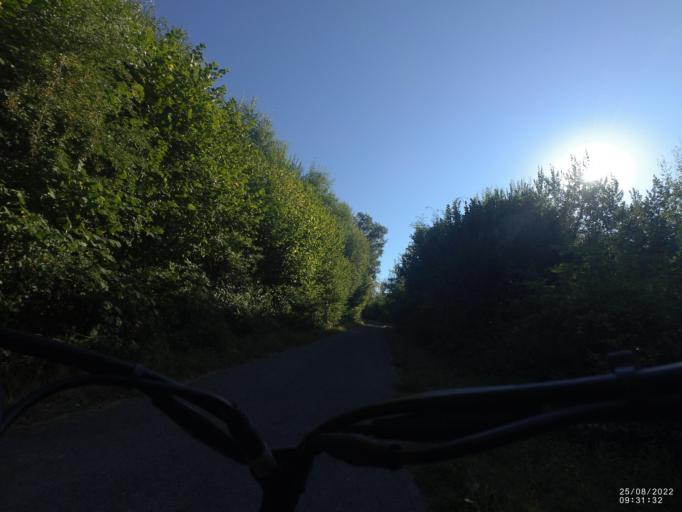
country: DE
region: Rheinland-Pfalz
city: Dohm-Lammersdorf
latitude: 50.2710
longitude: 6.6762
